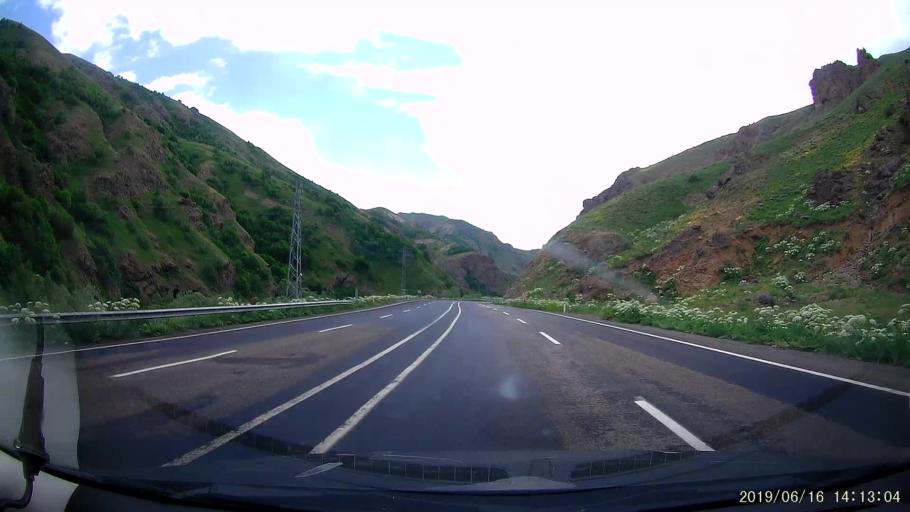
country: TR
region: Agri
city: Tahir
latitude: 39.7993
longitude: 42.5242
